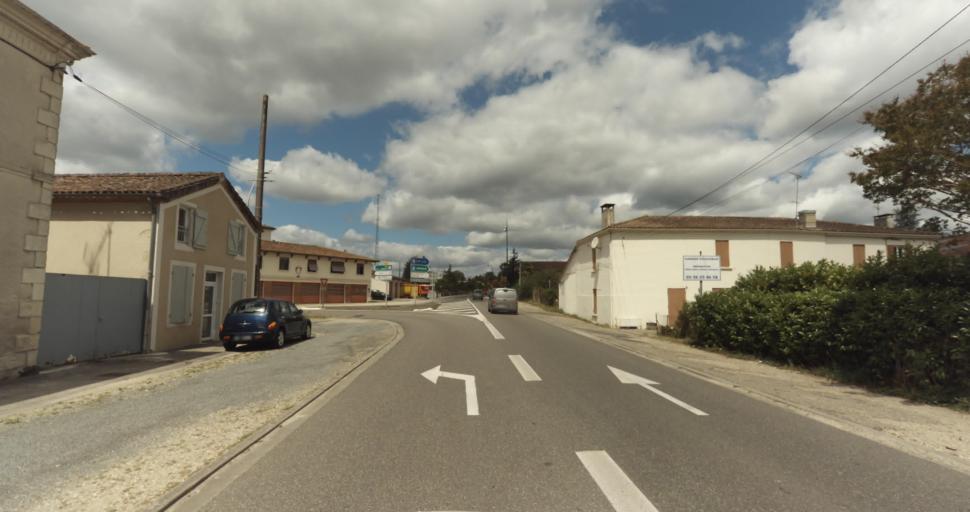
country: FR
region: Aquitaine
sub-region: Departement de la Gironde
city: Bazas
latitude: 44.4349
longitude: -0.2185
